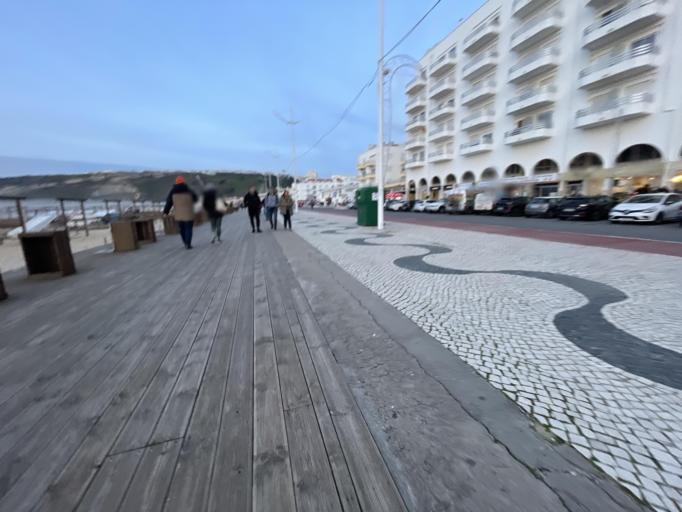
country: PT
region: Leiria
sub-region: Nazare
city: Nazare
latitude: 39.5955
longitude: -9.0725
